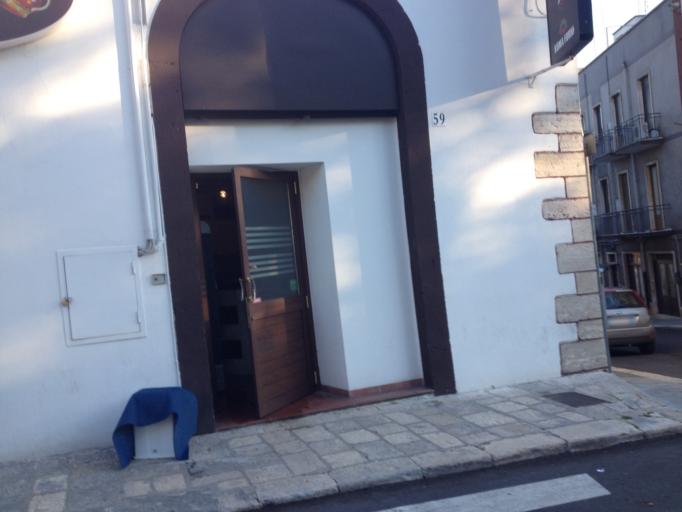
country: IT
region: Apulia
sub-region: Provincia di Bari
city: Putignano
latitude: 40.8476
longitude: 17.1207
